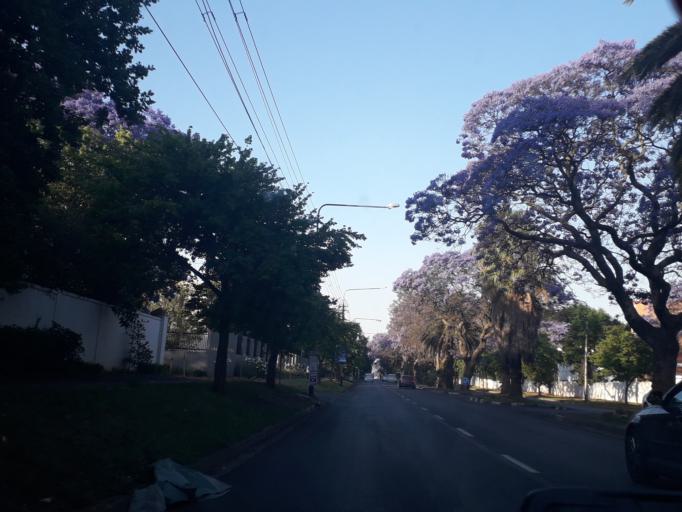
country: ZA
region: Gauteng
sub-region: City of Johannesburg Metropolitan Municipality
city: Johannesburg
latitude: -26.1402
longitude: 28.0446
